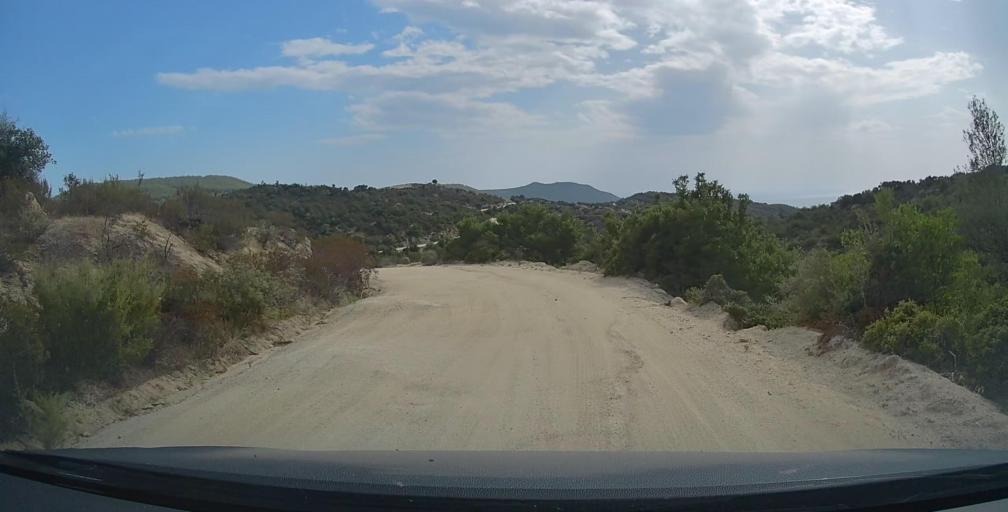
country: GR
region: Central Macedonia
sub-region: Nomos Chalkidikis
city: Sykia
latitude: 40.0011
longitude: 23.9260
